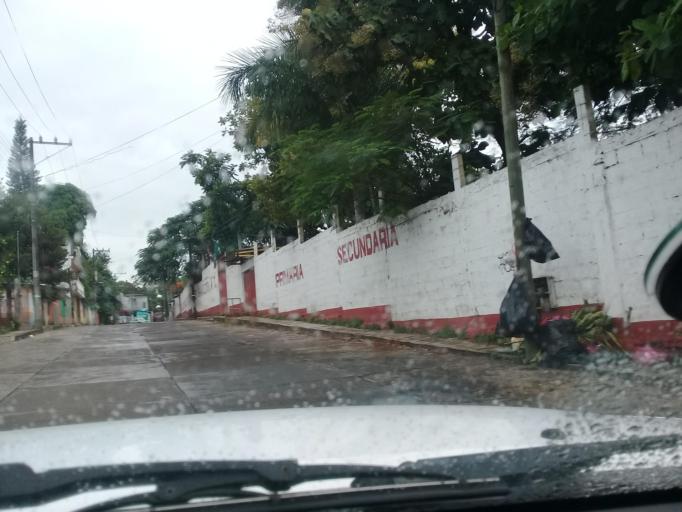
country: MX
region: Veracruz
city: San Andres Tuxtla
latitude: 18.4411
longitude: -95.2061
